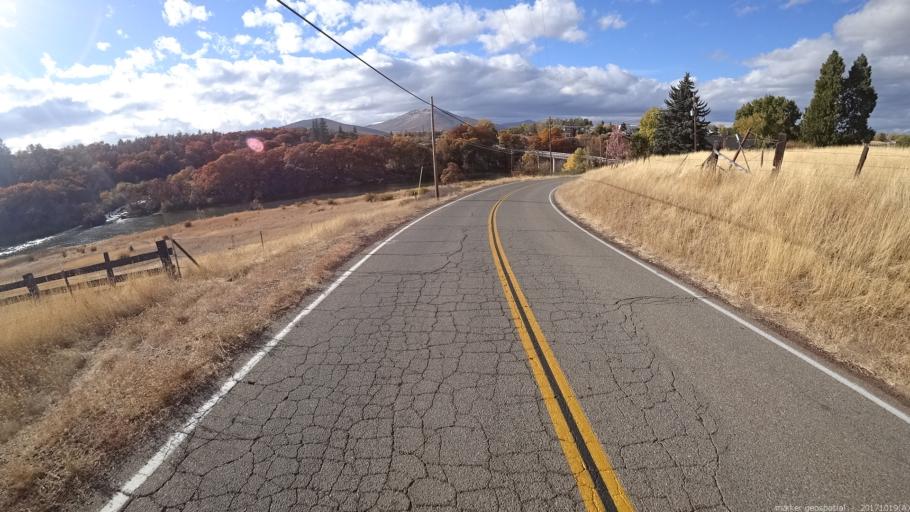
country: US
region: California
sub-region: Shasta County
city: Burney
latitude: 40.9998
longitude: -121.4343
